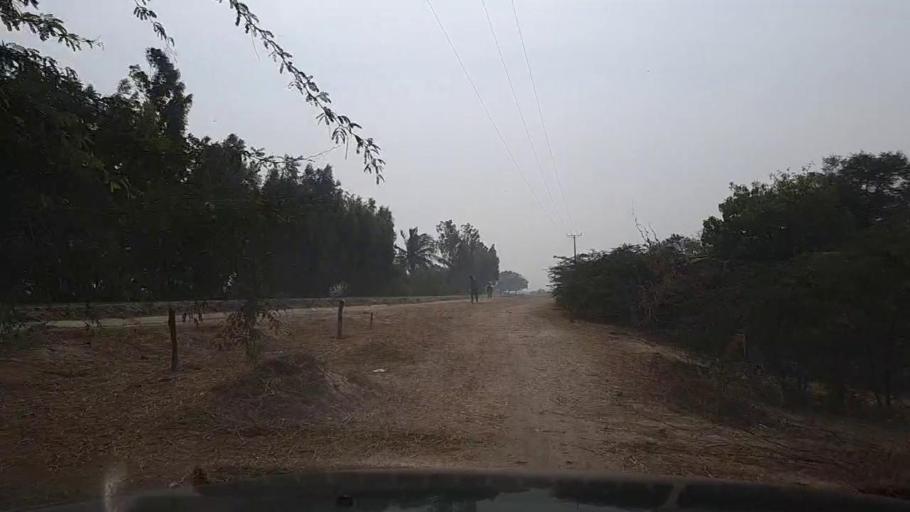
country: PK
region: Sindh
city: Mirpur Sakro
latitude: 24.5358
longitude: 67.8119
